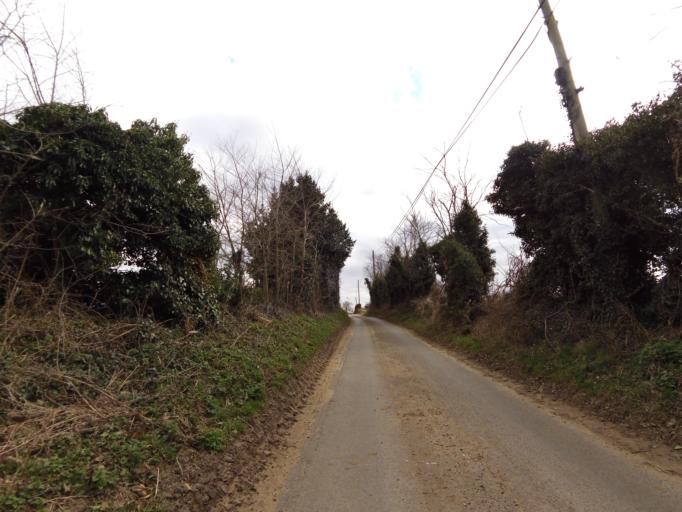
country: GB
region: England
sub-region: Suffolk
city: Woodbridge
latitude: 52.0475
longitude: 1.3271
